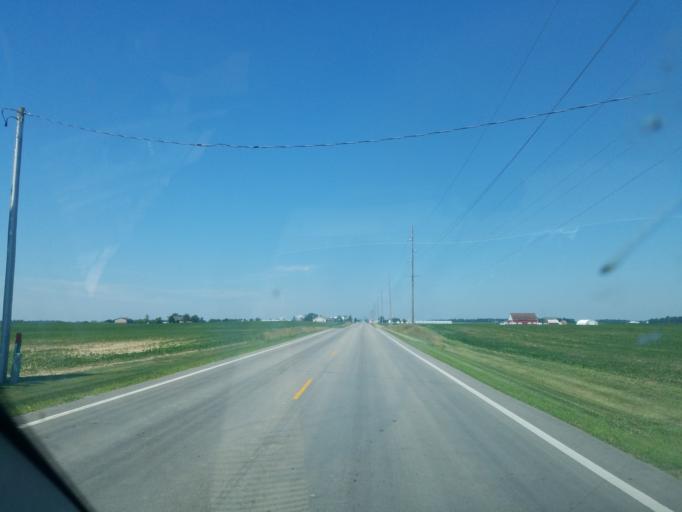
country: US
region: Ohio
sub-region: Auglaize County
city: New Bremen
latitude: 40.4368
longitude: -84.4271
